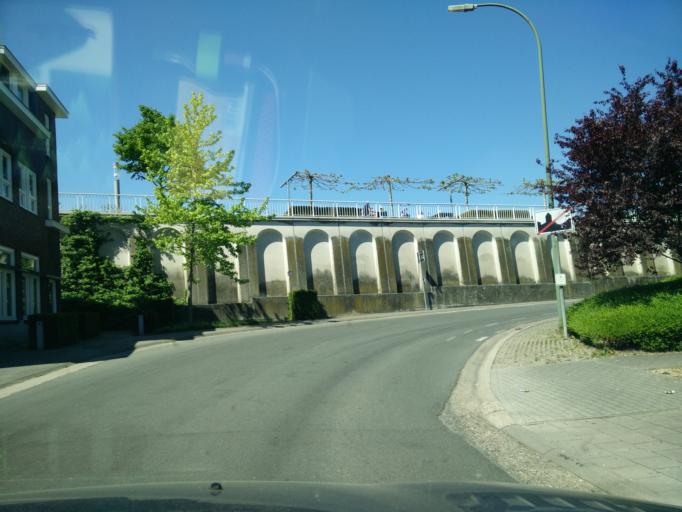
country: BE
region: Flanders
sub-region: Provincie Limburg
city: Maasmechelen
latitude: 50.9880
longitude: 5.7067
